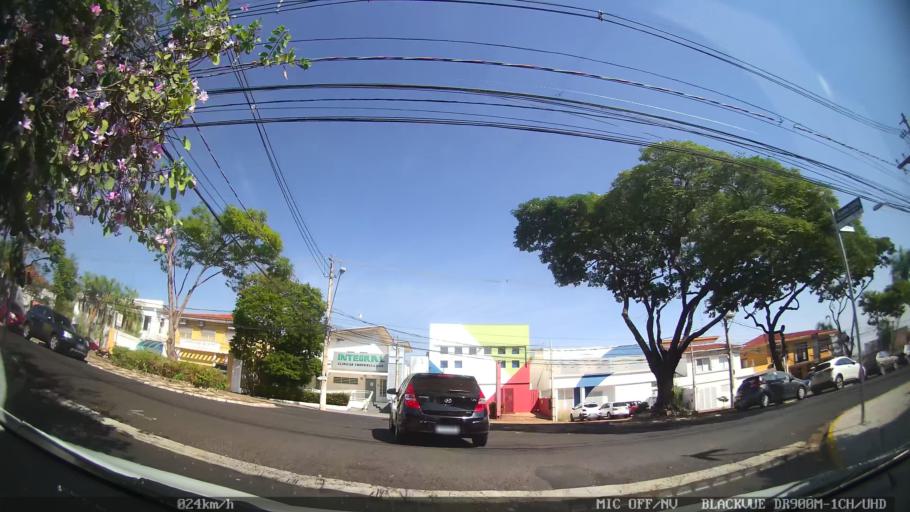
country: BR
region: Sao Paulo
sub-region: Ribeirao Preto
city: Ribeirao Preto
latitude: -21.1814
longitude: -47.8158
